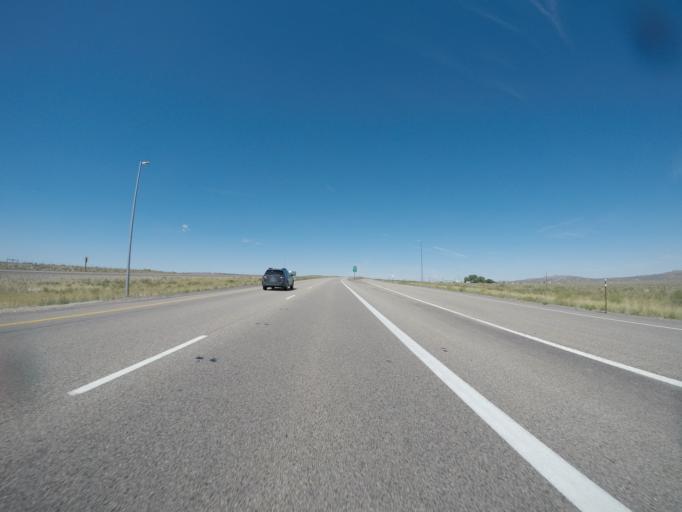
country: US
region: Wyoming
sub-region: Carbon County
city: Saratoga
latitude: 41.7415
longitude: -106.8233
